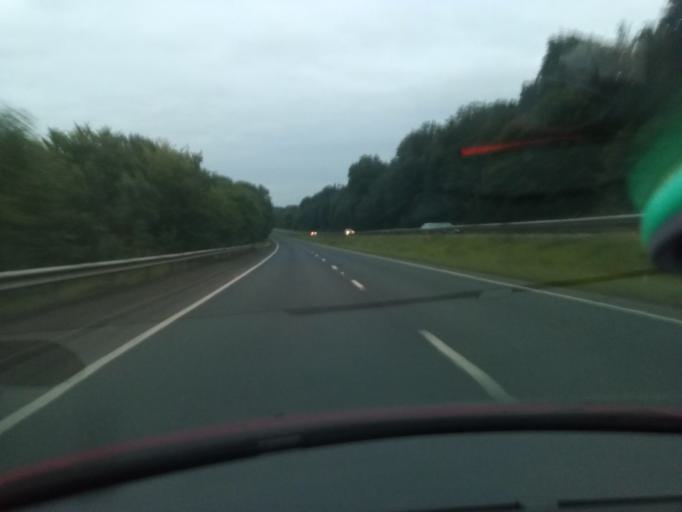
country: GB
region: England
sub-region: Northumberland
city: Acomb
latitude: 54.9851
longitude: -2.1203
